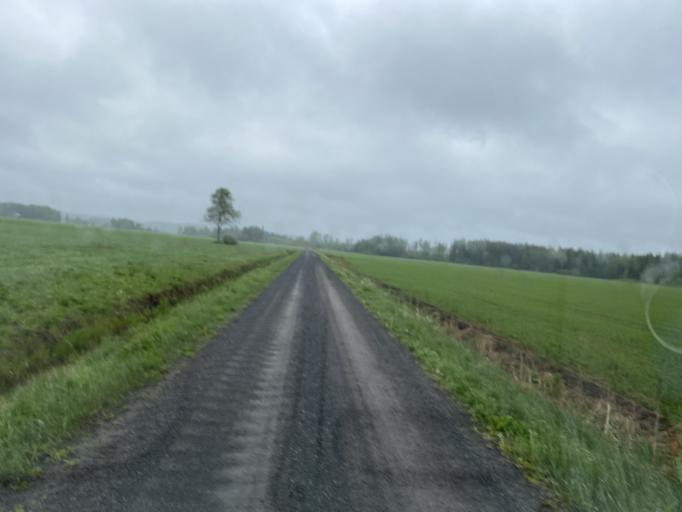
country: FI
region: Haeme
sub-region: Forssa
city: Forssa
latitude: 60.9482
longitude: 23.5946
